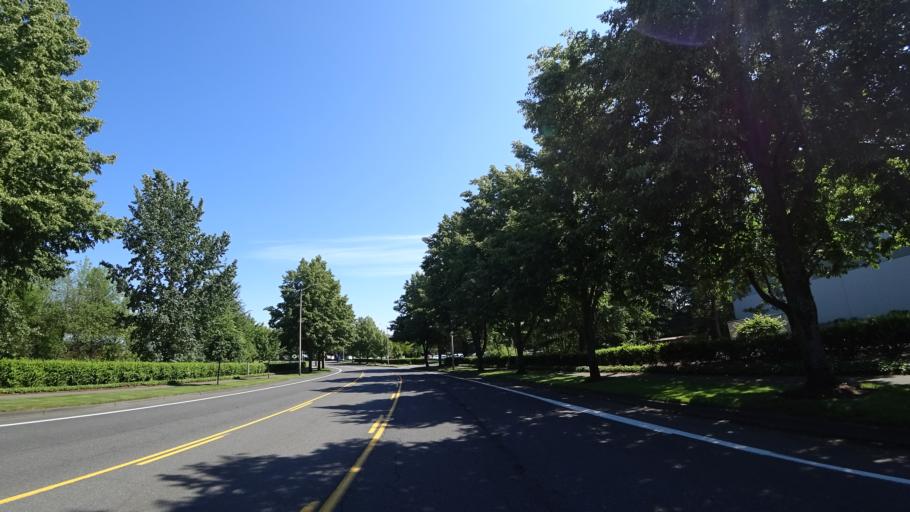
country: US
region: Oregon
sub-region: Multnomah County
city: Lents
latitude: 45.5732
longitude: -122.5746
